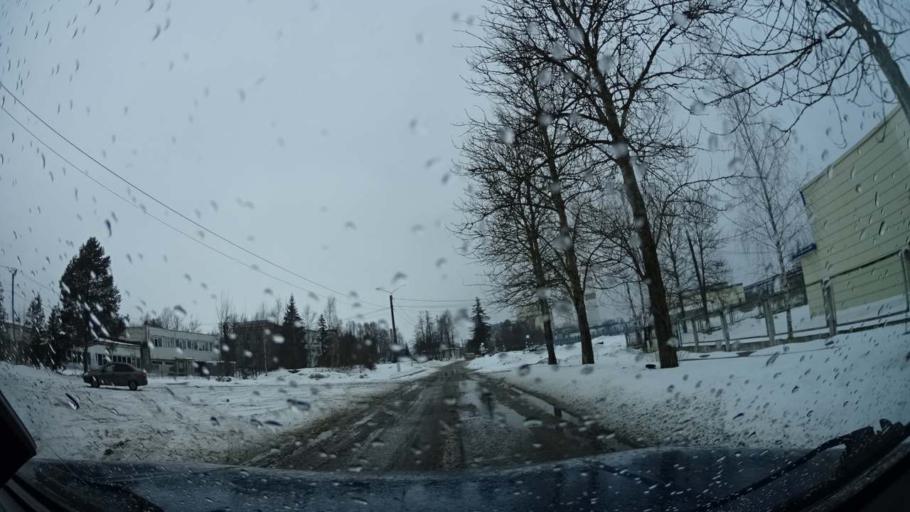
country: RU
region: Tverskaya
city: Konakovo
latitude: 56.7352
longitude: 36.7739
